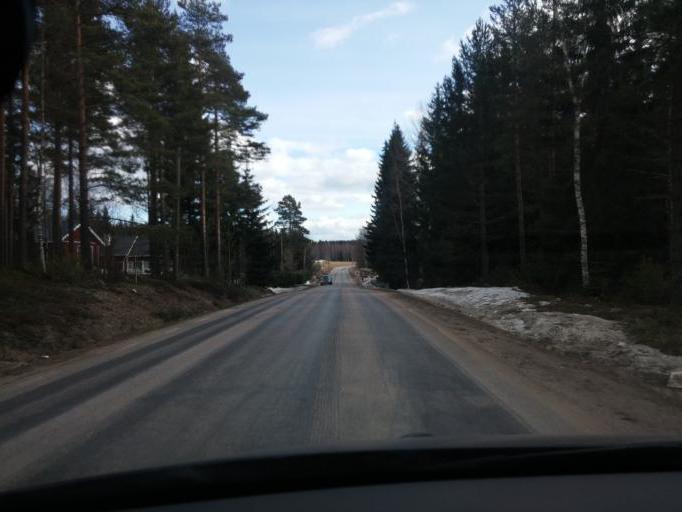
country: SE
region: Gaevleborg
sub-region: Ljusdals Kommun
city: Ljusdal
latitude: 61.8166
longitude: 16.1431
